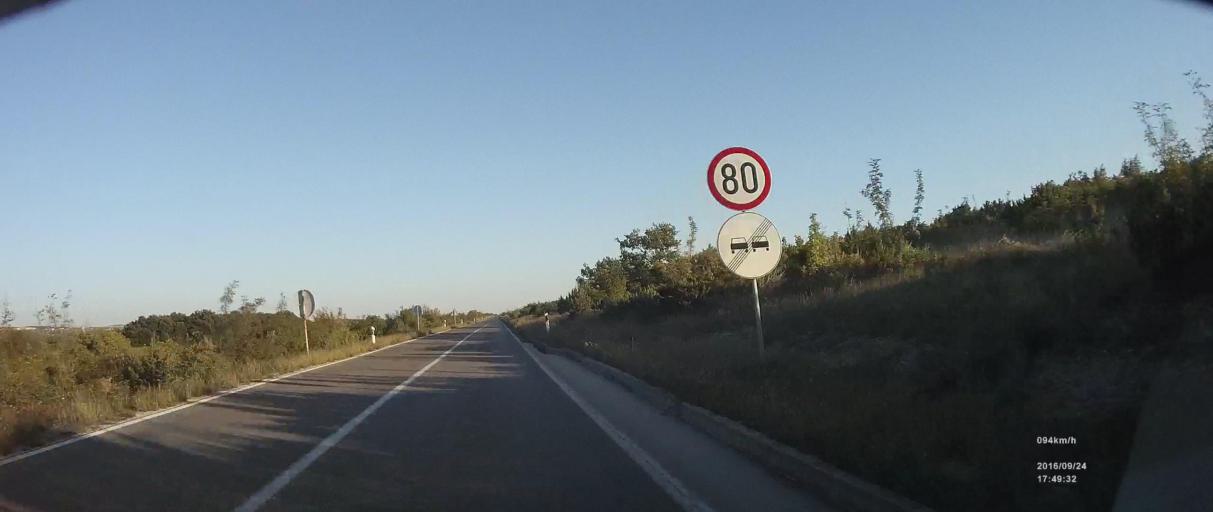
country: HR
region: Zadarska
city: Polaca
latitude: 44.0532
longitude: 15.5510
